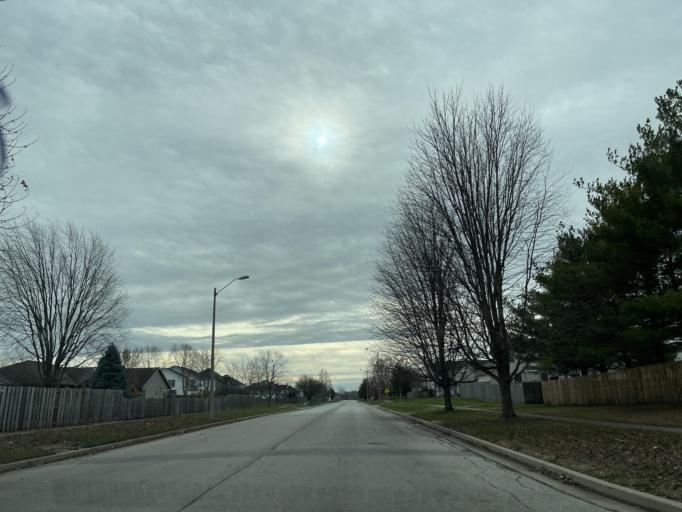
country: US
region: Illinois
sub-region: Sangamon County
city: Jerome
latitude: 39.7678
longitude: -89.7298
